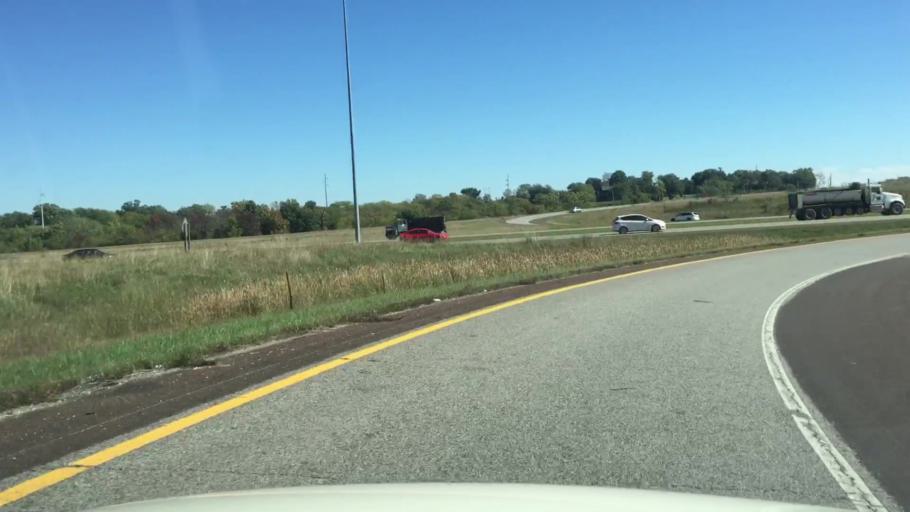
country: US
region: Kansas
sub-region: Wyandotte County
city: Edwardsville
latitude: 39.0122
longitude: -94.7862
